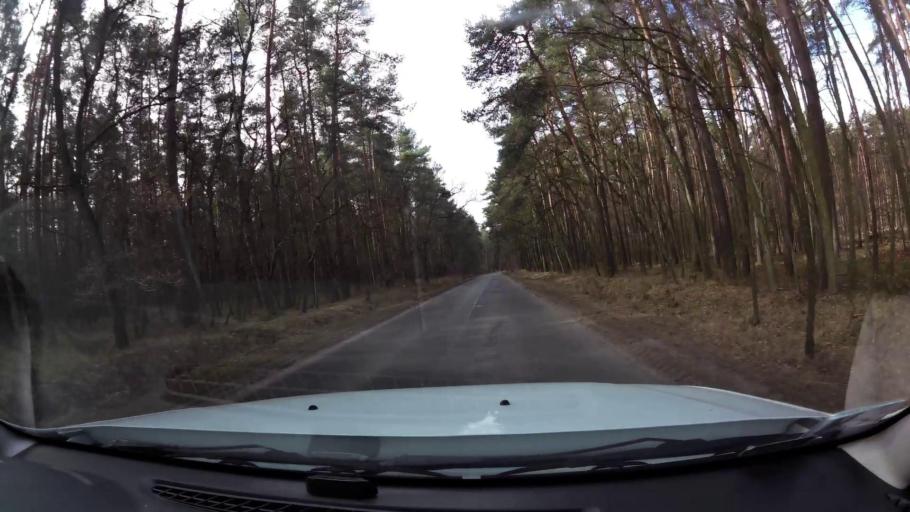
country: PL
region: West Pomeranian Voivodeship
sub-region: Powiat mysliborski
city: Debno
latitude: 52.8310
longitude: 14.6575
